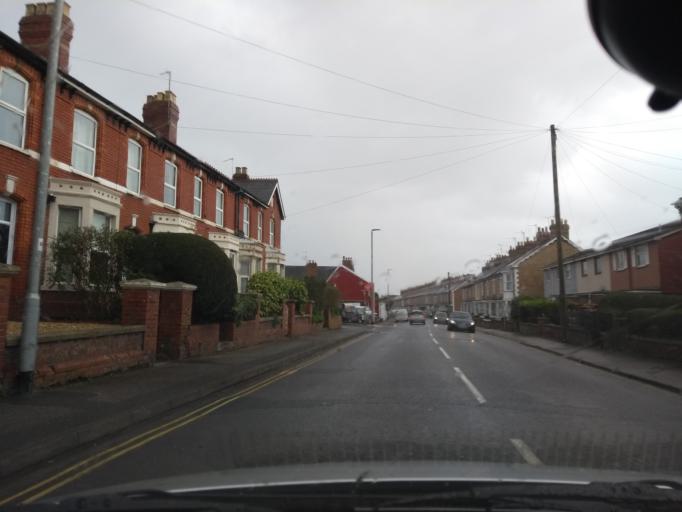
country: GB
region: England
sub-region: Somerset
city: Taunton
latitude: 51.0271
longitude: -3.1084
